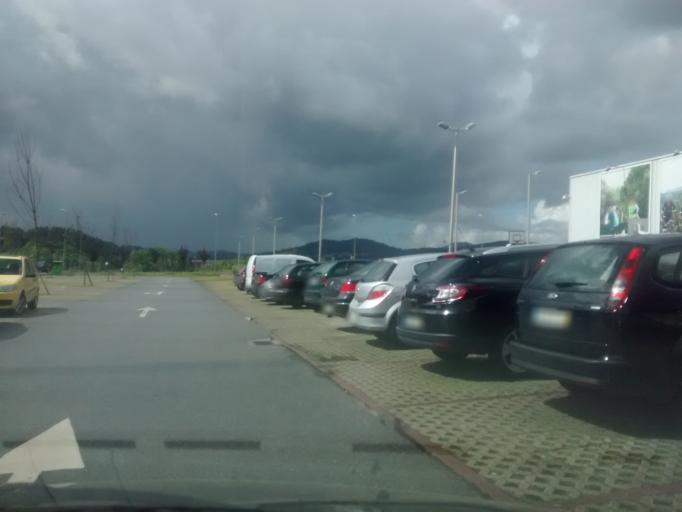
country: PT
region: Braga
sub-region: Braga
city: Braga
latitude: 41.5701
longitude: -8.4281
